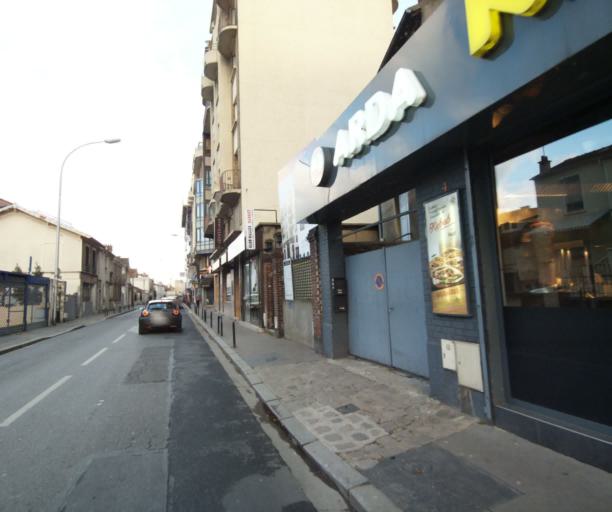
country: FR
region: Ile-de-France
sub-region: Departement des Hauts-de-Seine
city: La Defense
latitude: 48.8979
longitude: 2.2406
